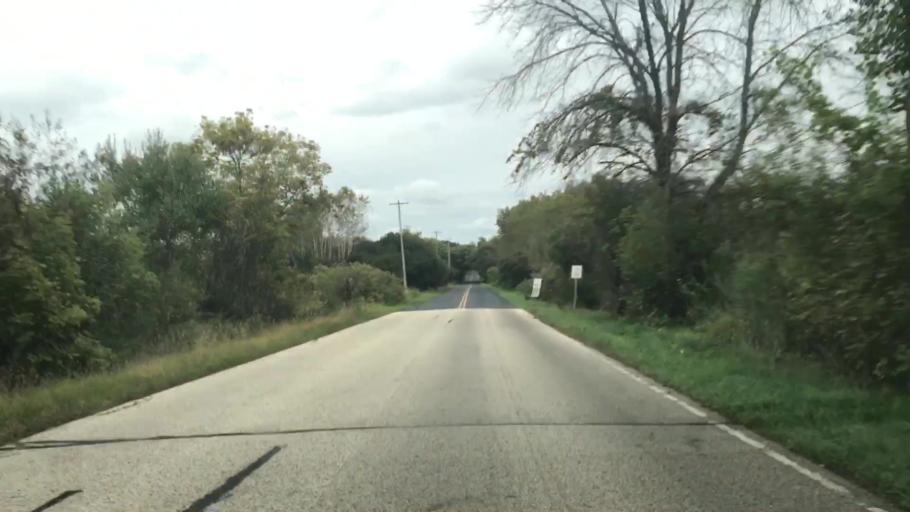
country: US
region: Wisconsin
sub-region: Waukesha County
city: North Prairie
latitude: 42.9152
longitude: -88.4250
